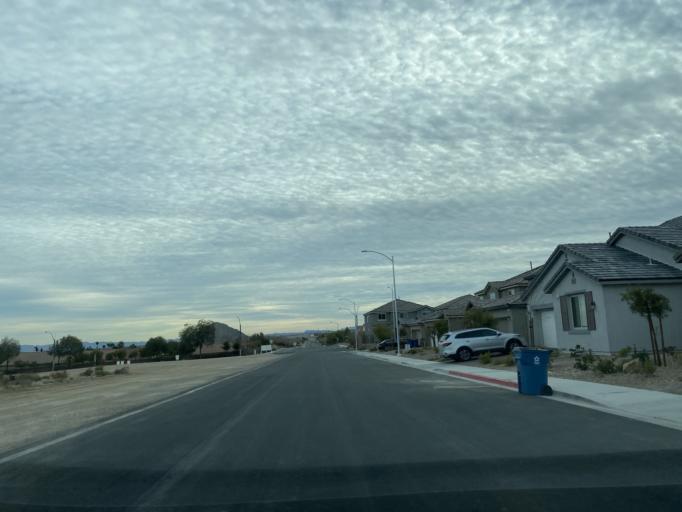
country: US
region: Nevada
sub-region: Clark County
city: Summerlin South
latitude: 36.2785
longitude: -115.3242
